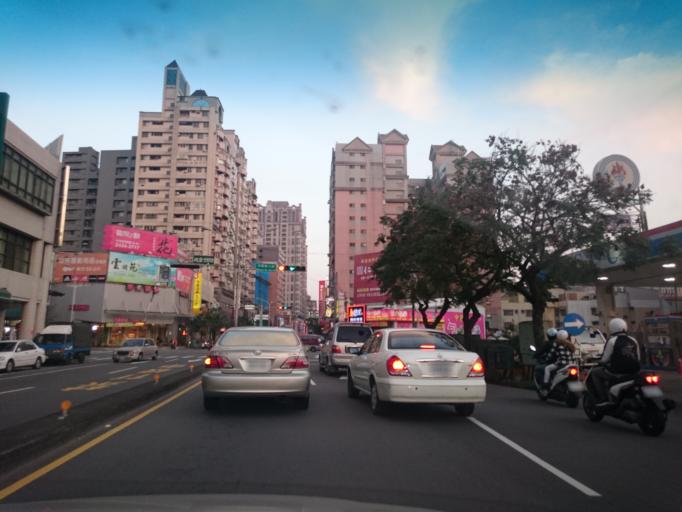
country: TW
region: Taiwan
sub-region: Taichung City
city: Taichung
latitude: 24.1715
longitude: 120.6438
